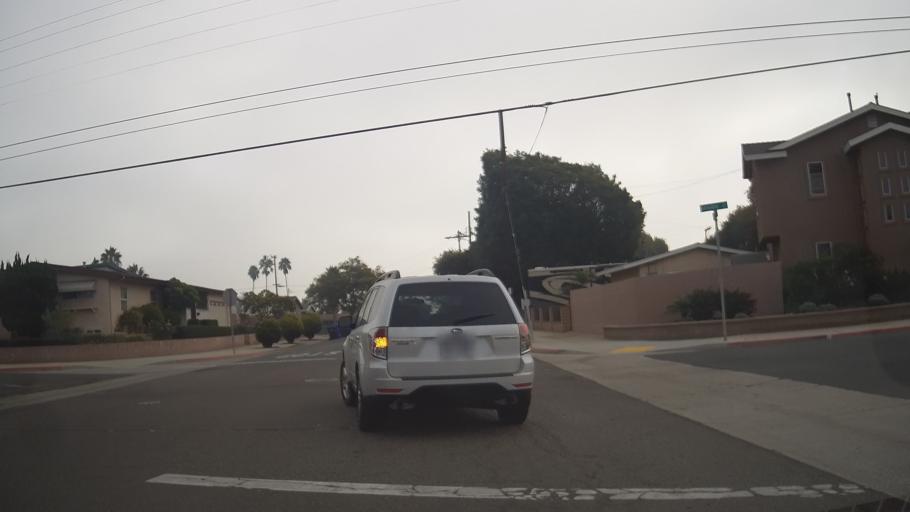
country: US
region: California
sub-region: San Diego County
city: San Diego
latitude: 32.7983
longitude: -117.1421
